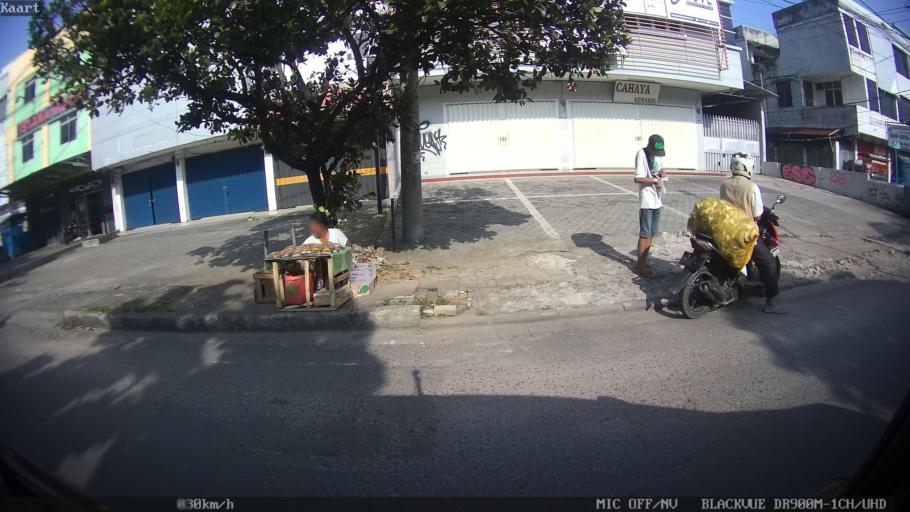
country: ID
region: Lampung
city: Kedaton
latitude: -5.3968
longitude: 105.2614
